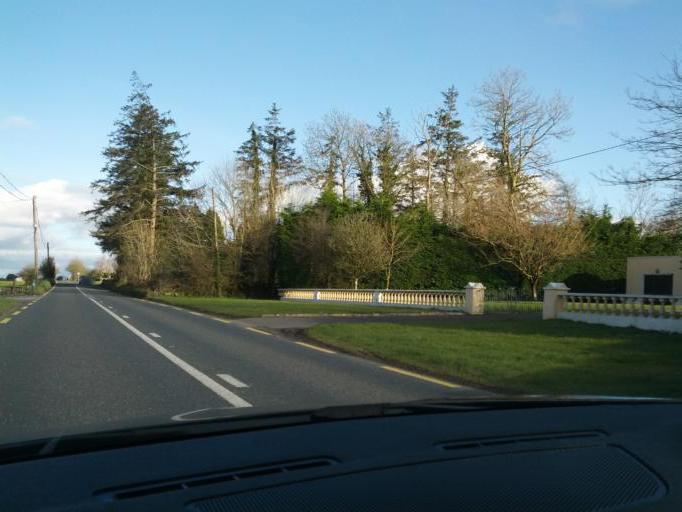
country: IE
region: Connaught
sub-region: Roscommon
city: Roscommon
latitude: 53.6516
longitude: -8.2443
